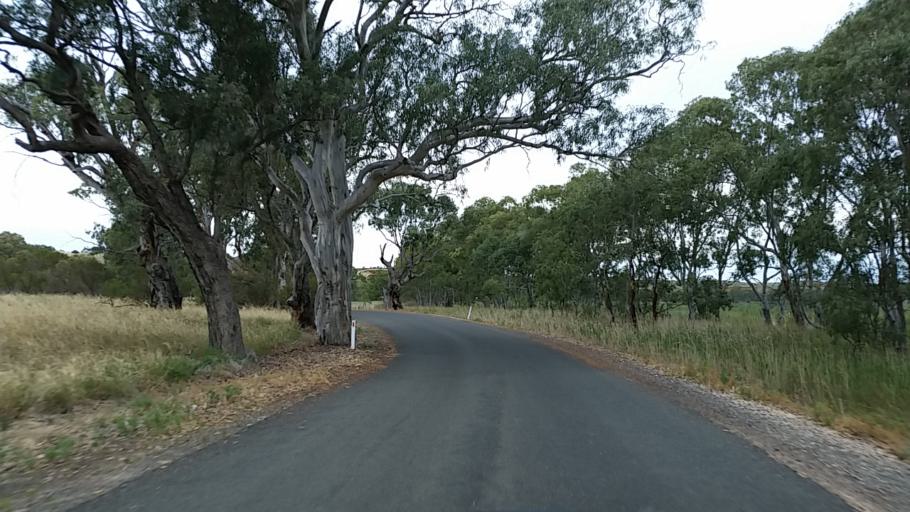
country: AU
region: South Australia
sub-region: Mid Murray
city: Mannum
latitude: -34.7543
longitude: 139.5640
